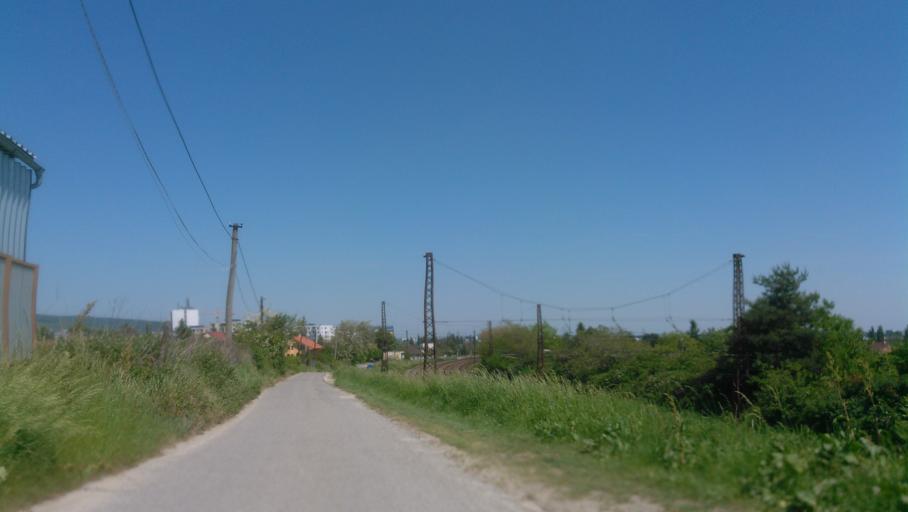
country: SK
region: Bratislavsky
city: Bratislava
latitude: 48.1840
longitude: 17.1265
